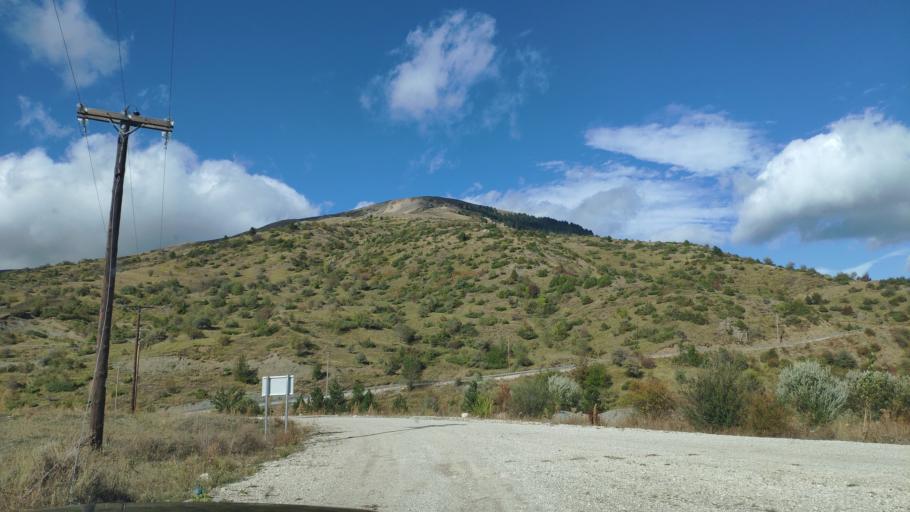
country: AL
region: Korce
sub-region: Rrethi i Devollit
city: Miras
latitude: 40.3951
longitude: 20.8369
